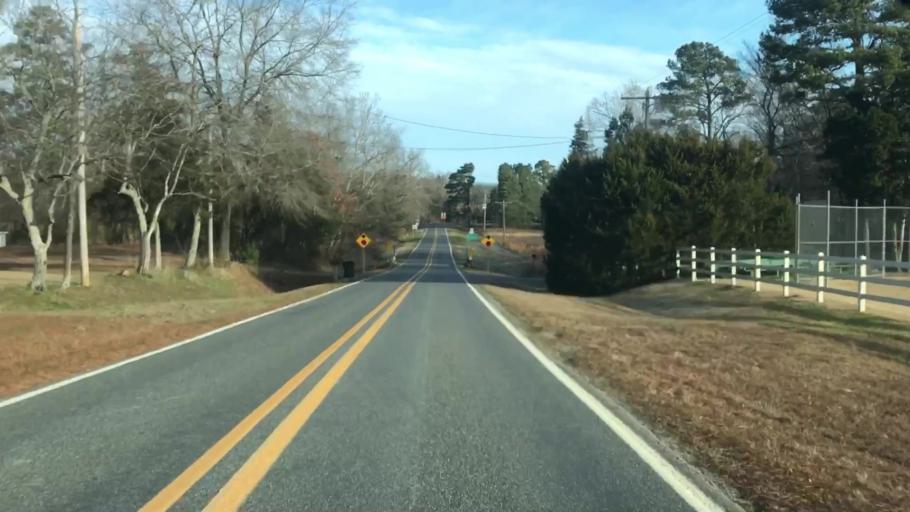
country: US
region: Arkansas
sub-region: Garland County
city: Rockwell
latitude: 34.5079
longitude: -93.2761
